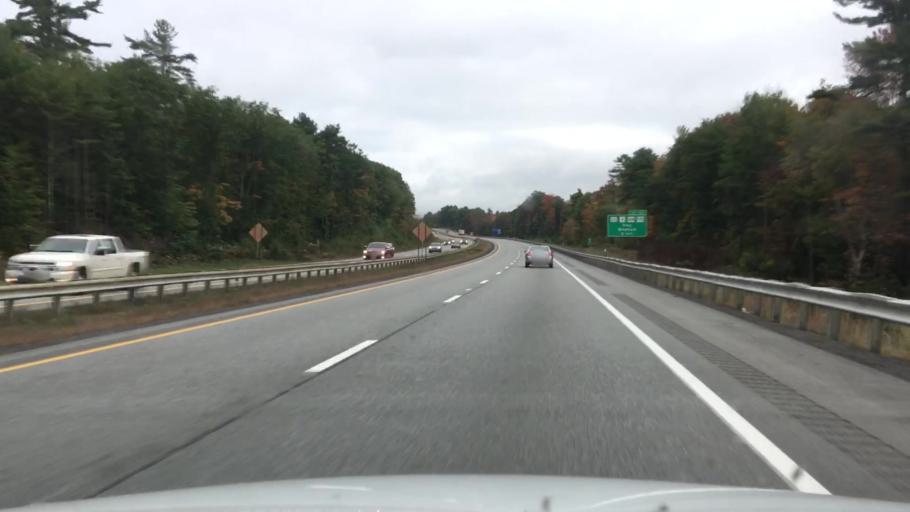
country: US
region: Maine
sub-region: Cumberland County
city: Cumberland Center
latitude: 43.8519
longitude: -70.3229
